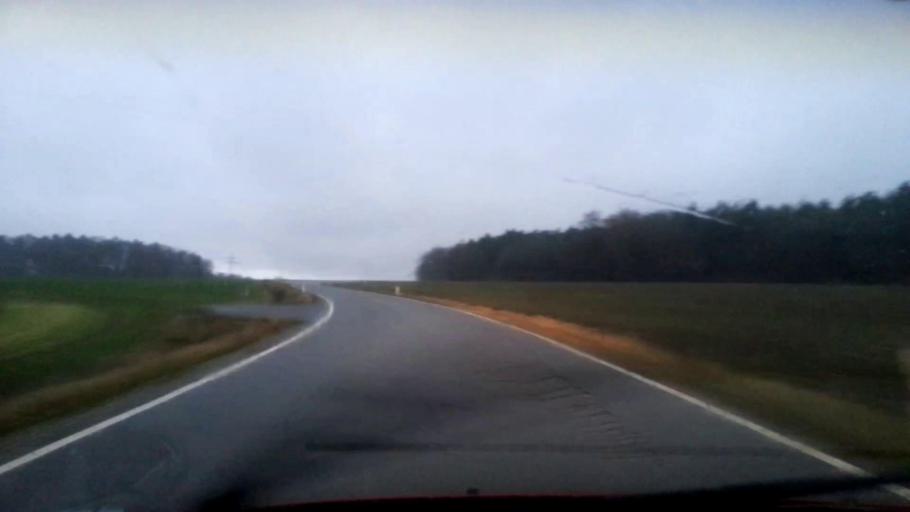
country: DE
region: Bavaria
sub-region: Upper Franconia
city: Konigsfeld
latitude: 49.9602
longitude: 11.1433
